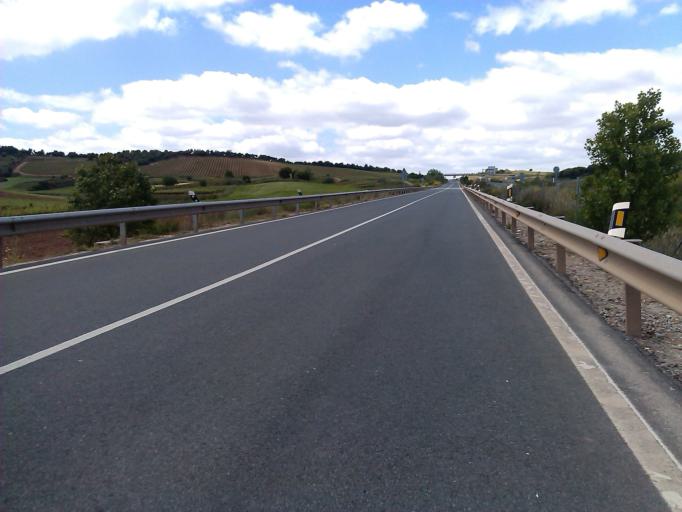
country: ES
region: La Rioja
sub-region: Provincia de La Rioja
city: Ventosa
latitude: 42.4136
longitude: -2.6301
